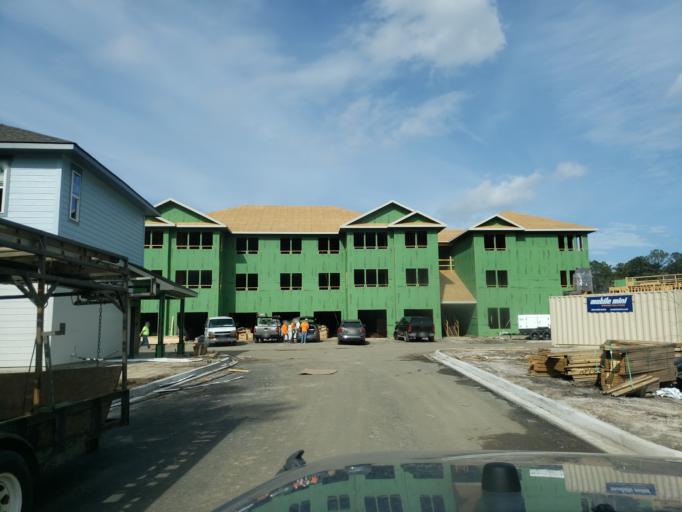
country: US
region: Georgia
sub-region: Chatham County
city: Pooler
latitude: 32.1707
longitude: -81.2315
